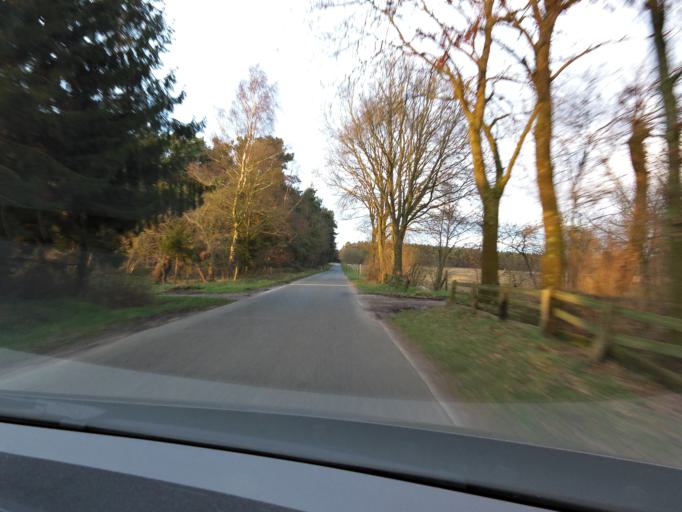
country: DE
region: Schleswig-Holstein
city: Seedorf
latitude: 53.6290
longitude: 10.8594
